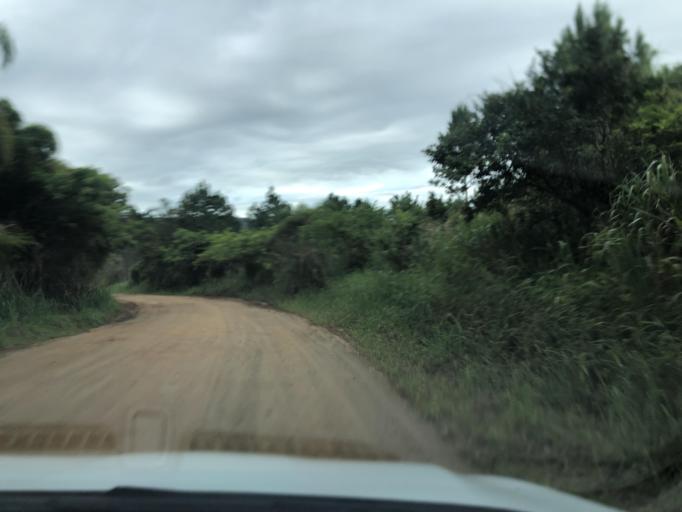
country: BR
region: Santa Catarina
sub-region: Florianopolis
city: Itacorubi
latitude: -27.5457
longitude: -48.4437
